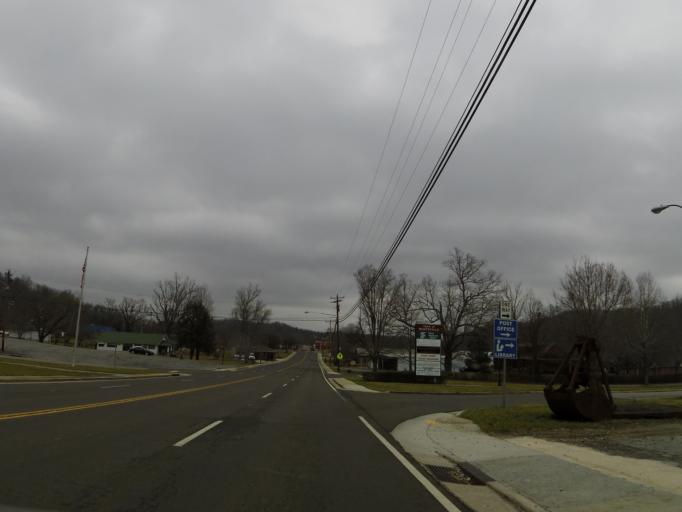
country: US
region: Tennessee
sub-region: Scott County
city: Huntsville
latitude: 36.4119
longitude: -84.4918
